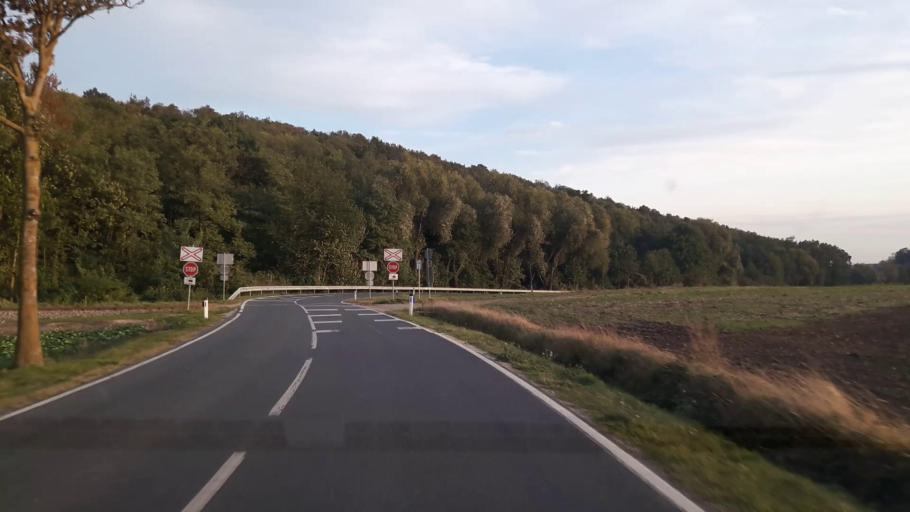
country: AT
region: Lower Austria
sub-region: Politischer Bezirk Korneuburg
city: Ernstbrunn
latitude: 48.4912
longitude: 16.3696
